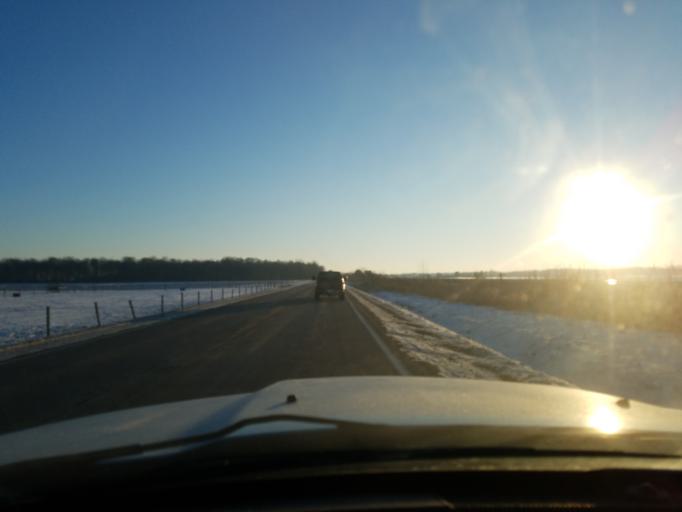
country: US
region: Indiana
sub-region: Elkhart County
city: Nappanee
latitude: 41.4461
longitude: -86.0657
